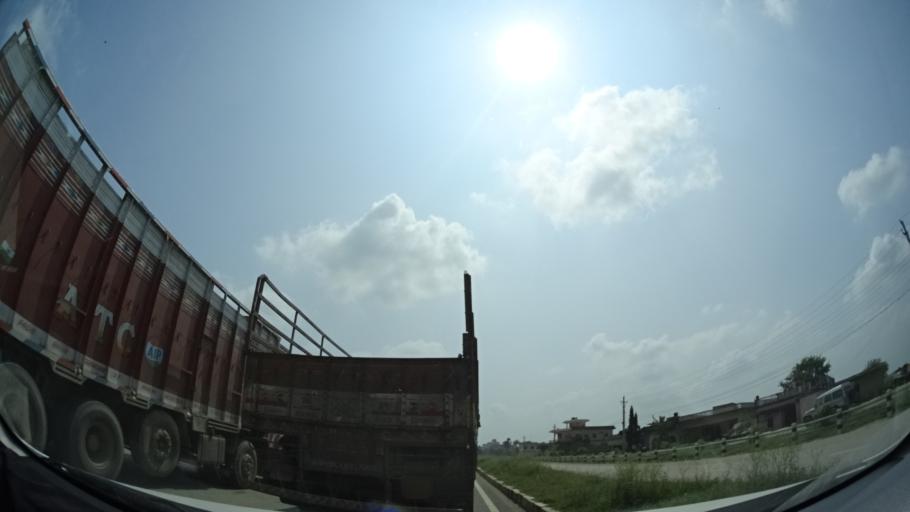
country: NP
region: Western Region
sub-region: Lumbini Zone
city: Bhairahawa
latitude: 27.4827
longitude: 83.4602
